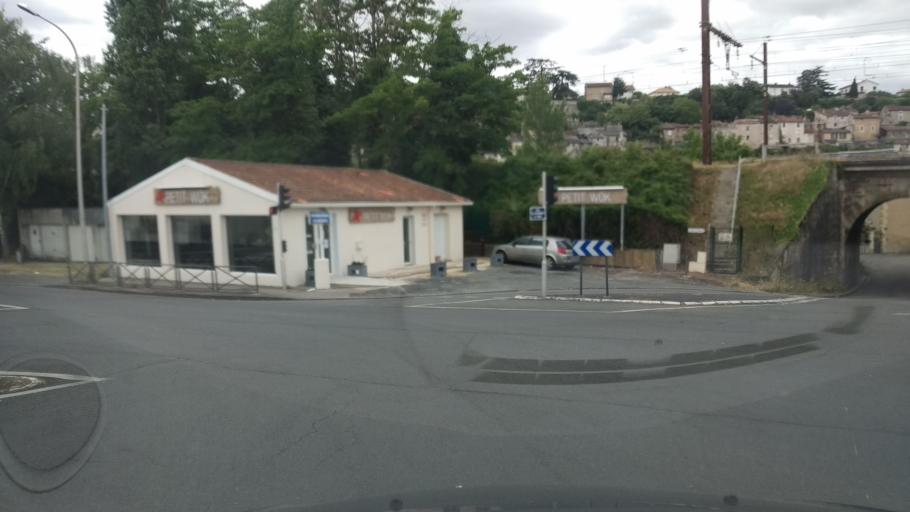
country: FR
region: Poitou-Charentes
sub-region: Departement de la Vienne
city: Poitiers
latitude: 46.5926
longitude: 0.3404
